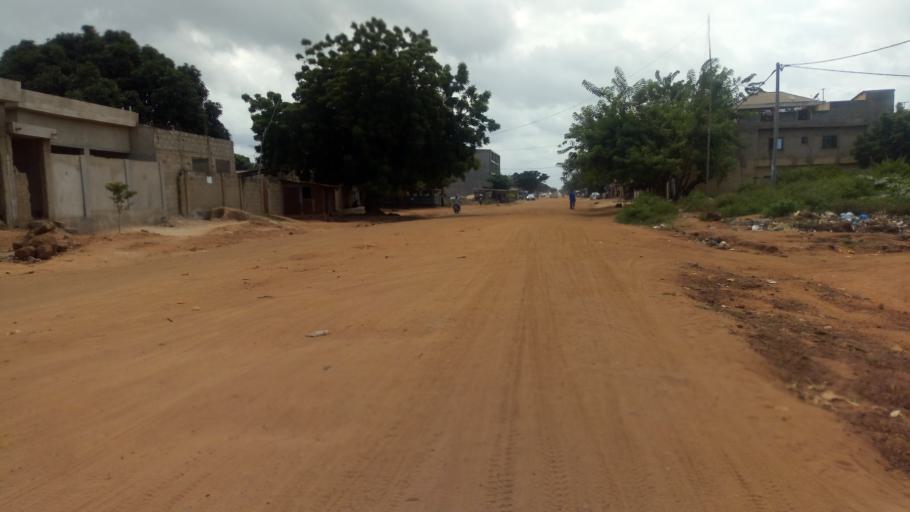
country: TG
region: Maritime
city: Lome
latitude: 6.2218
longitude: 1.1807
